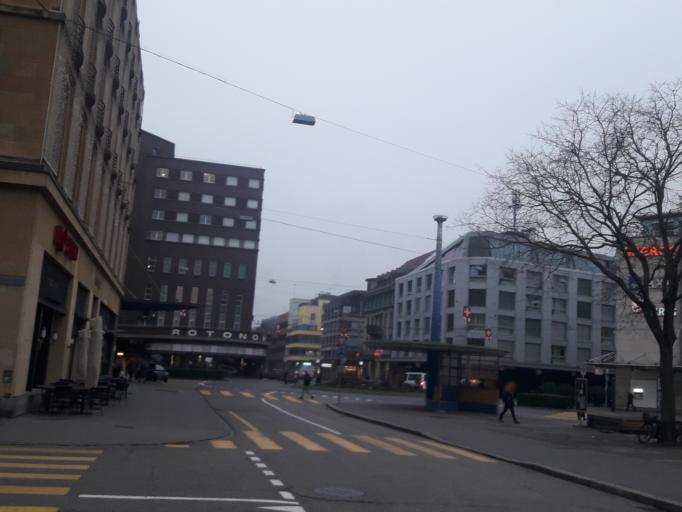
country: CH
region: Bern
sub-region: Biel/Bienne District
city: Biel/Bienne
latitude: 47.1347
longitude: 7.2450
